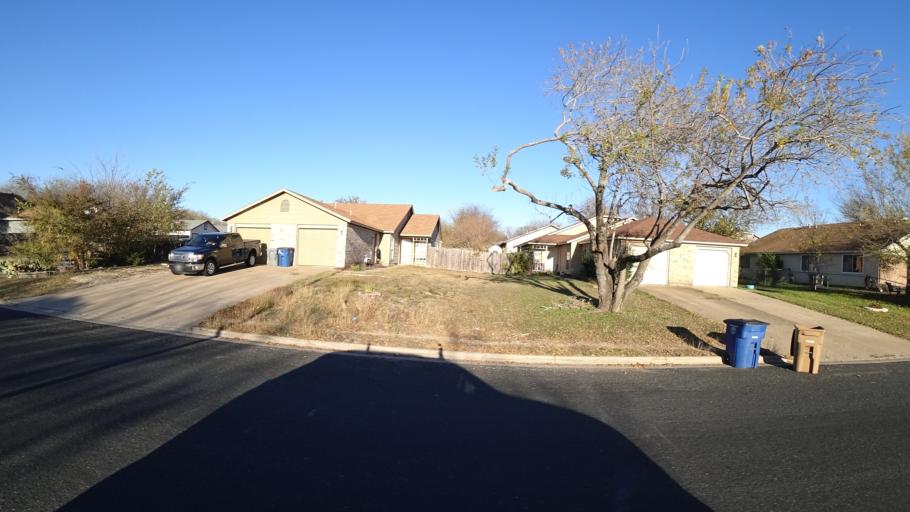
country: US
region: Texas
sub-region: Travis County
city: Wells Branch
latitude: 30.4108
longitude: -97.7003
